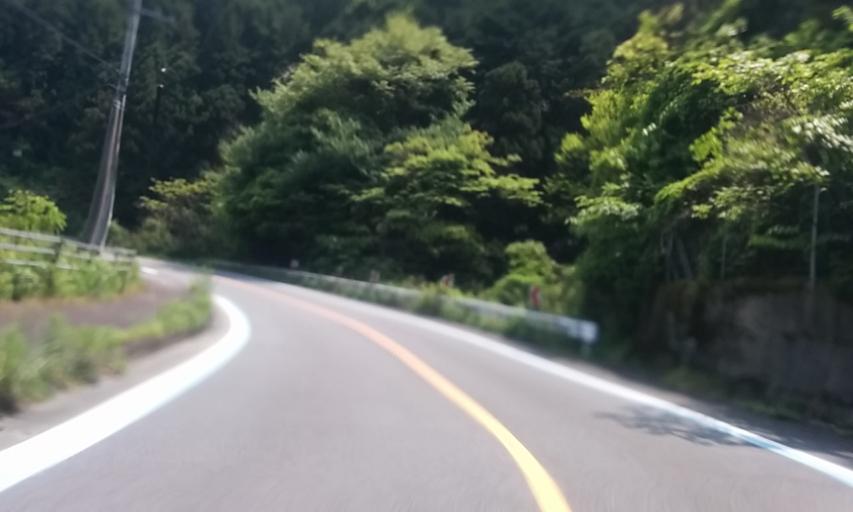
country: JP
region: Ehime
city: Saijo
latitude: 33.8491
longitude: 133.2069
